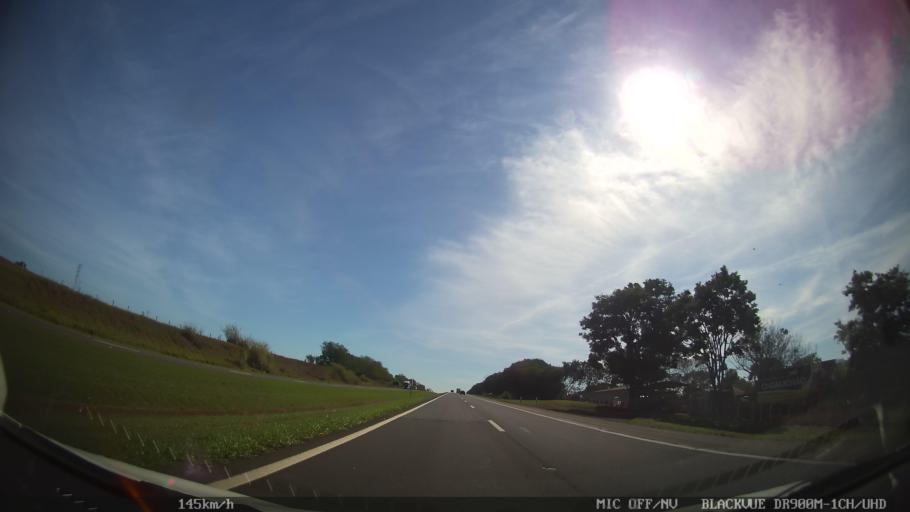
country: BR
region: Sao Paulo
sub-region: Leme
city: Leme
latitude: -22.1276
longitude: -47.4097
